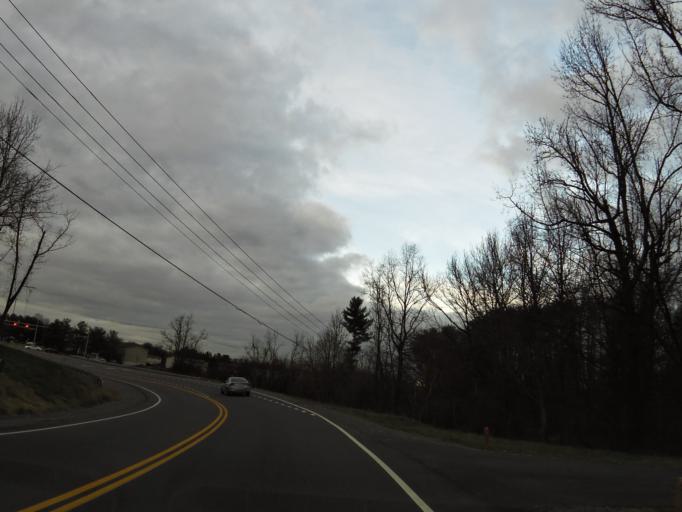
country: US
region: Tennessee
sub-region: Blount County
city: Alcoa
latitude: 35.8463
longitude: -83.9887
